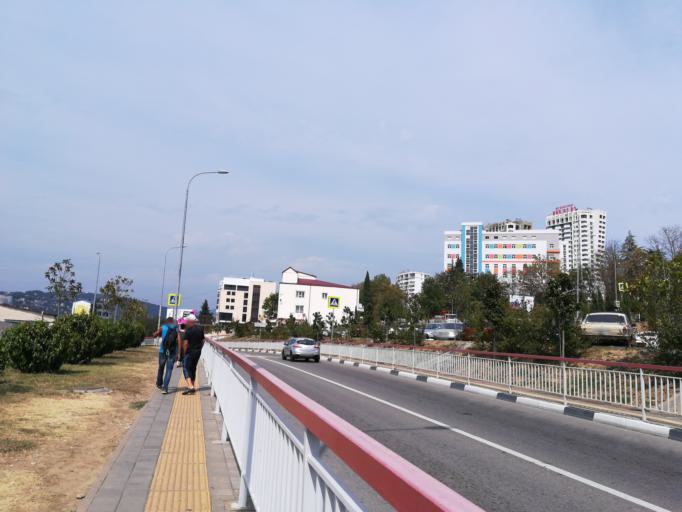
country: RU
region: Krasnodarskiy
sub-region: Sochi City
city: Sochi
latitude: 43.5978
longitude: 39.7320
